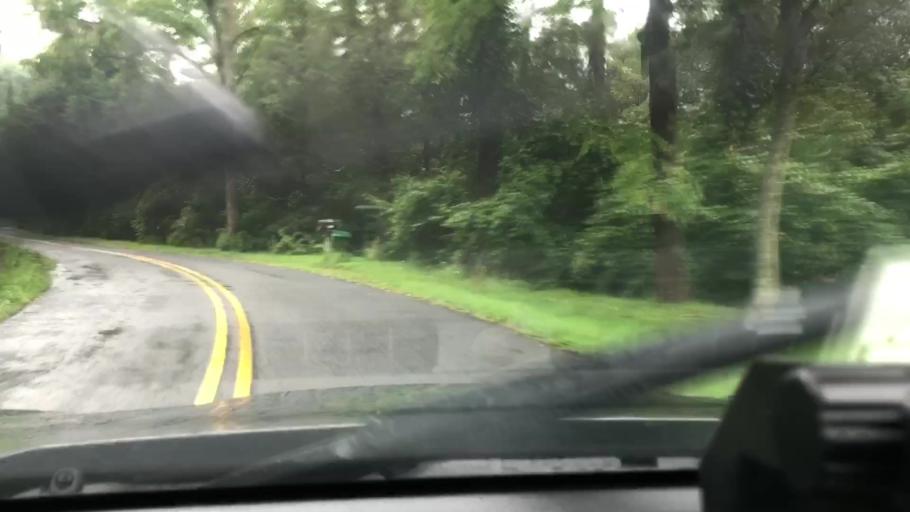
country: US
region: Pennsylvania
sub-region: Lehigh County
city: Macungie
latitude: 40.4729
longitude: -75.5495
